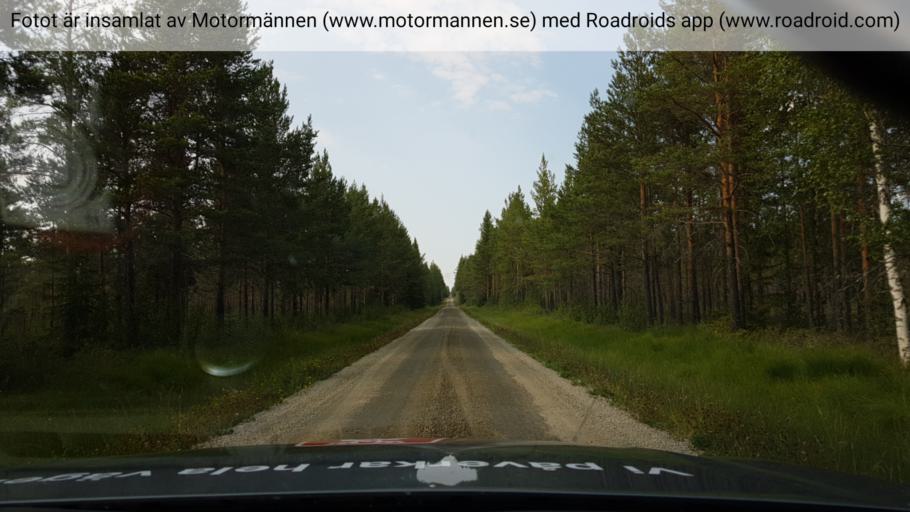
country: SE
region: Jaemtland
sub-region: Braecke Kommun
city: Braecke
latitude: 62.4975
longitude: 14.9213
